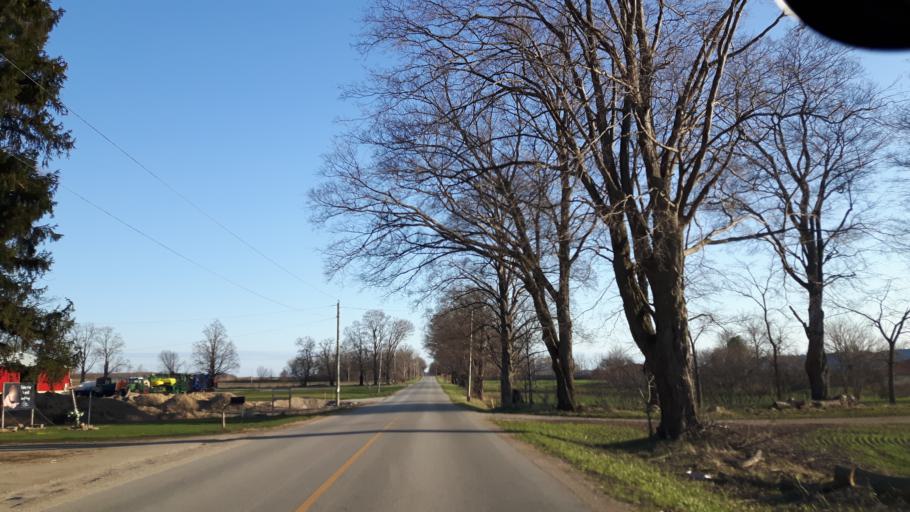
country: CA
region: Ontario
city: Goderich
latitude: 43.7044
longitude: -81.6850
